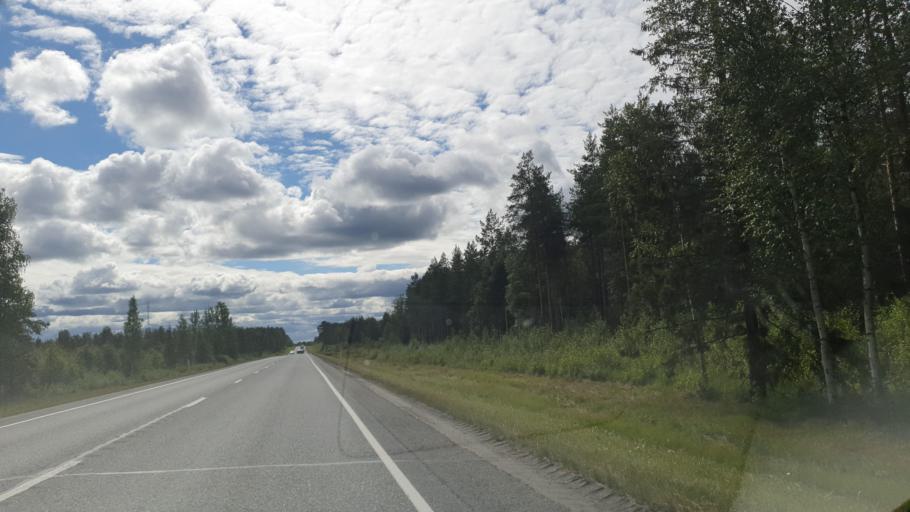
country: FI
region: Kainuu
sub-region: Kajaani
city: Kajaani
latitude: 64.1344
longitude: 27.4872
